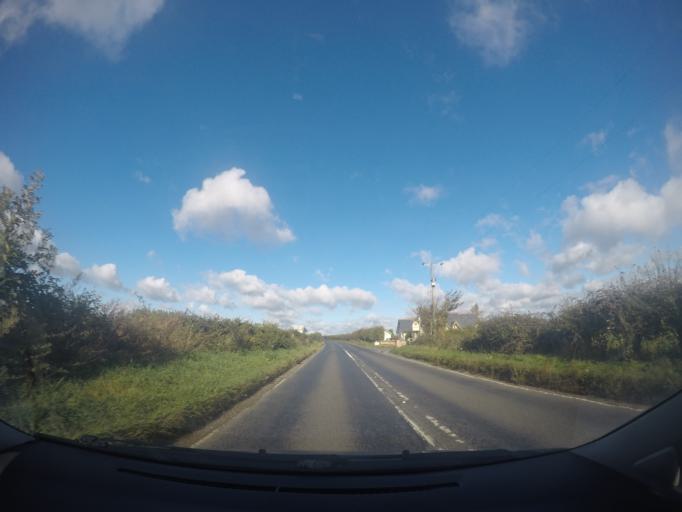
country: GB
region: England
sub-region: City and Borough of Leeds
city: Walton
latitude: 54.0185
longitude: -1.3119
